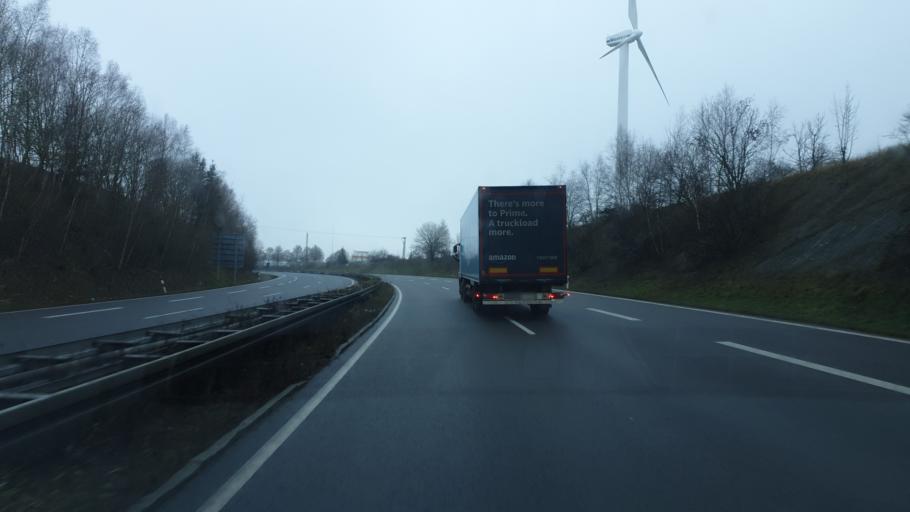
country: DE
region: Saxony
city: Gornau
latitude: 50.7524
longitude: 13.0366
